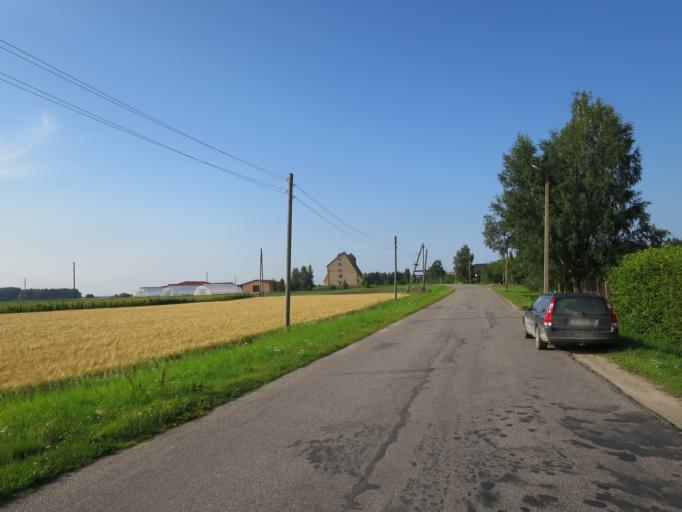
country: LV
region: Priekuli
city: Priekuli
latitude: 57.3109
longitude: 25.3395
